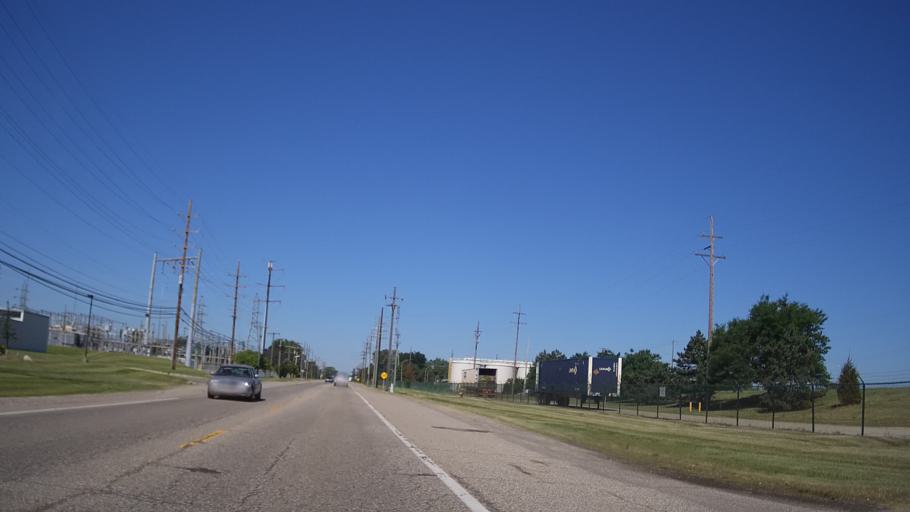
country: US
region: Michigan
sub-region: Macomb County
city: Sterling Heights
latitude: 42.5948
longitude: -83.0369
